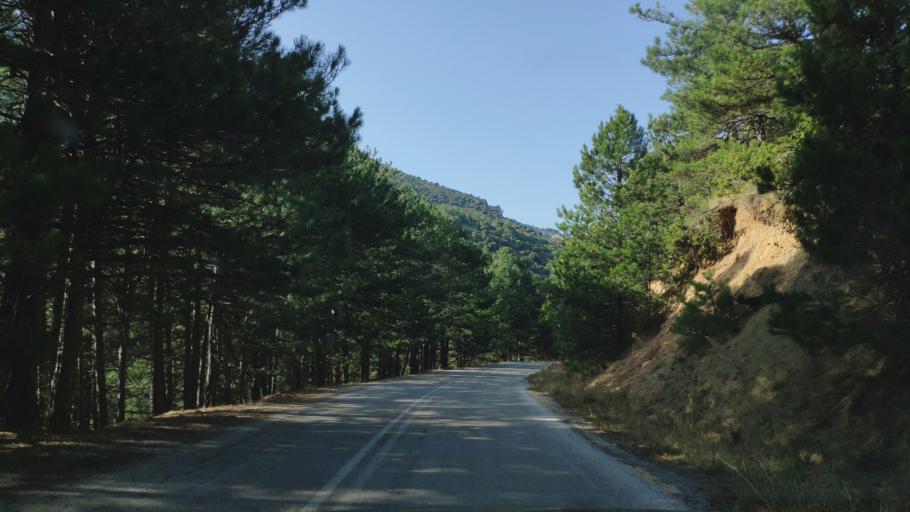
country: GR
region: West Greece
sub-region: Nomos Achaias
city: Aiyira
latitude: 38.0532
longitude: 22.3820
